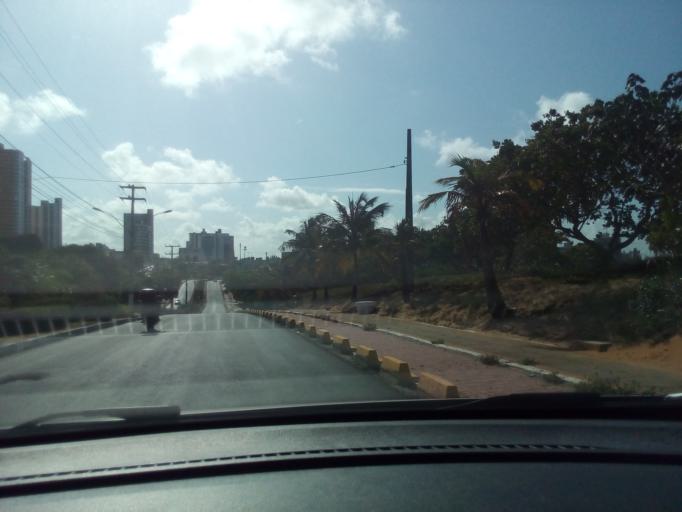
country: BR
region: Rio Grande do Norte
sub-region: Natal
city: Natal
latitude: -5.8379
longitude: -35.2077
